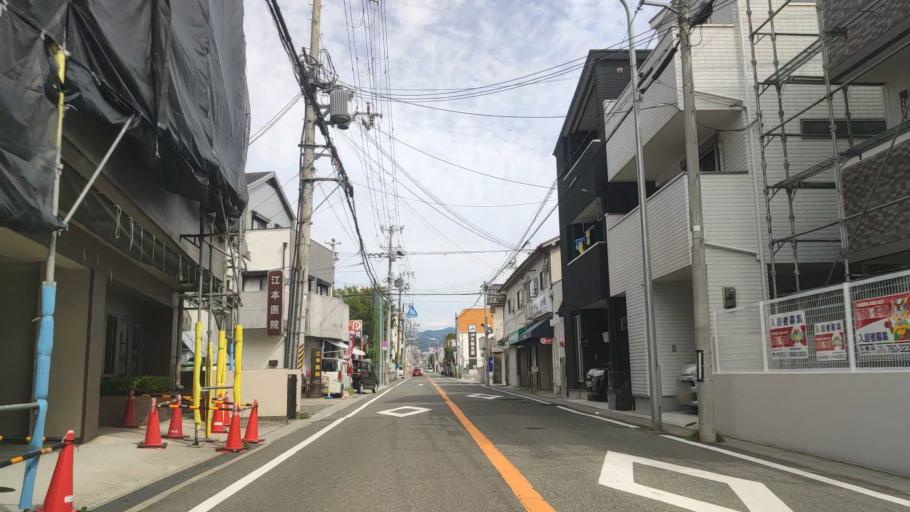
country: JP
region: Osaka
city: Toyonaka
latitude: 34.8021
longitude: 135.4635
